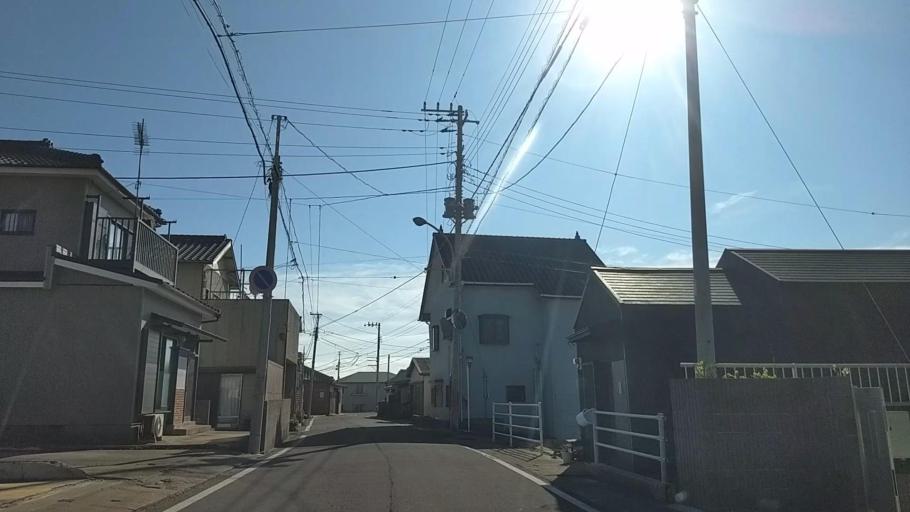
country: JP
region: Chiba
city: Hasaki
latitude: 35.6971
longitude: 140.8551
